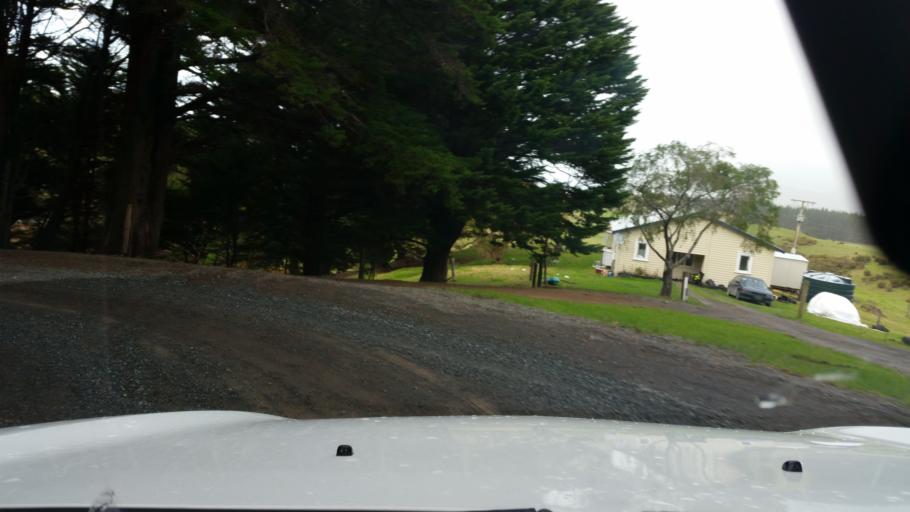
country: NZ
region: Northland
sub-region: Whangarei
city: Ruakaka
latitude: -35.7778
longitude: 174.5423
